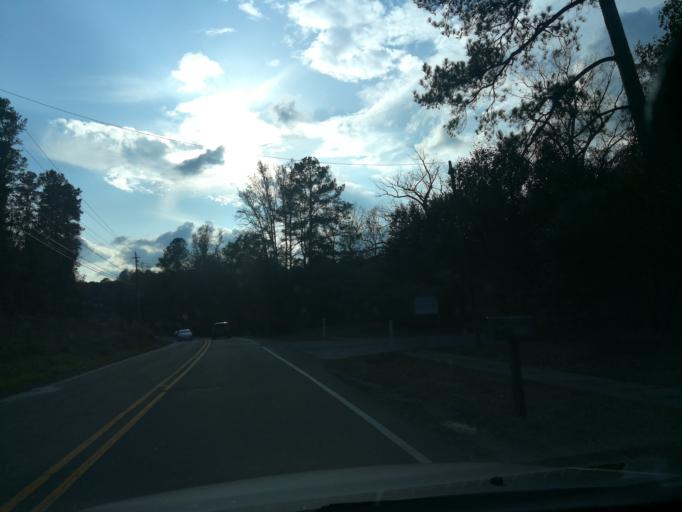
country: US
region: North Carolina
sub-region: Orange County
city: Chapel Hill
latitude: 35.9848
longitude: -78.9942
